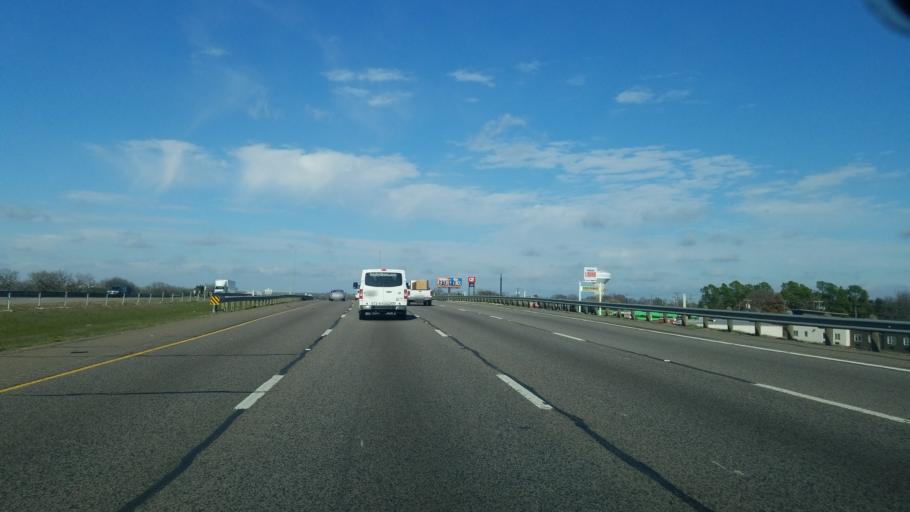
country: US
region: Texas
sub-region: Dallas County
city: Balch Springs
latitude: 32.7337
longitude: -96.6120
